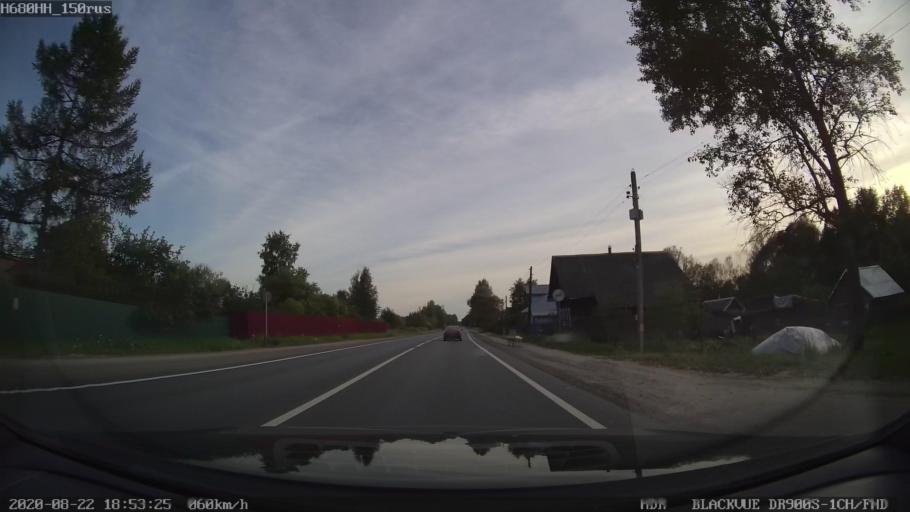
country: RU
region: Tverskaya
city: Rameshki
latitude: 57.2257
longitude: 36.0976
